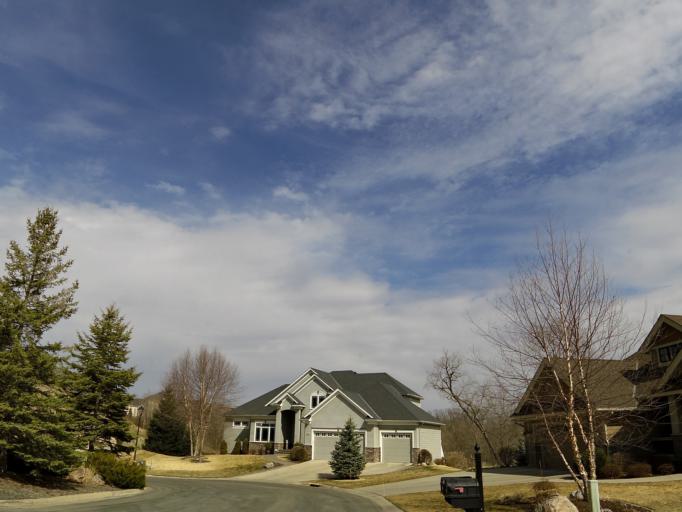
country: US
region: Minnesota
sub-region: Scott County
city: Prior Lake
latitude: 44.7340
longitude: -93.4523
